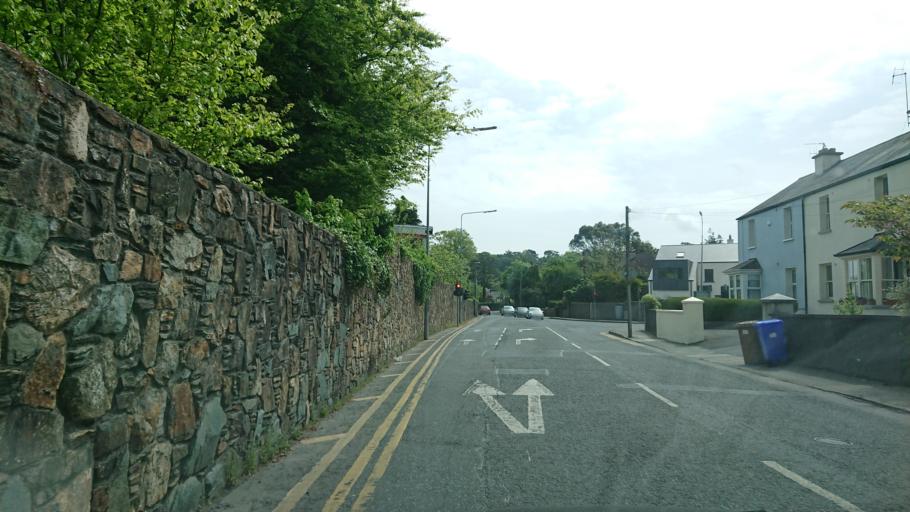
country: IE
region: Munster
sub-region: Waterford
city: Waterford
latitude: 52.2505
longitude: -7.1009
